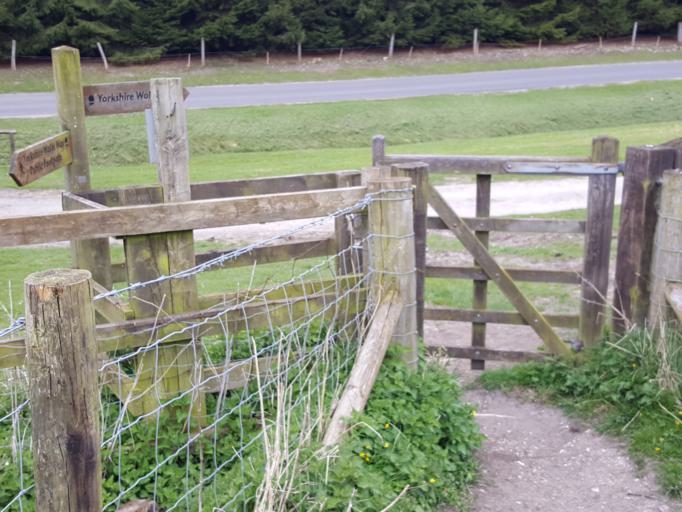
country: GB
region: England
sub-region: East Riding of Yorkshire
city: Brantingham
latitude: 53.7574
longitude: -0.5706
